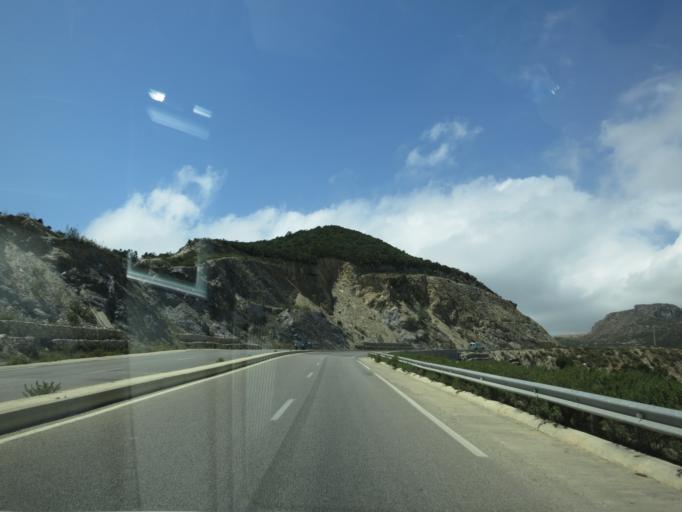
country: ES
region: Ceuta
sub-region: Ceuta
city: Ceuta
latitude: 35.8681
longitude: -5.3808
